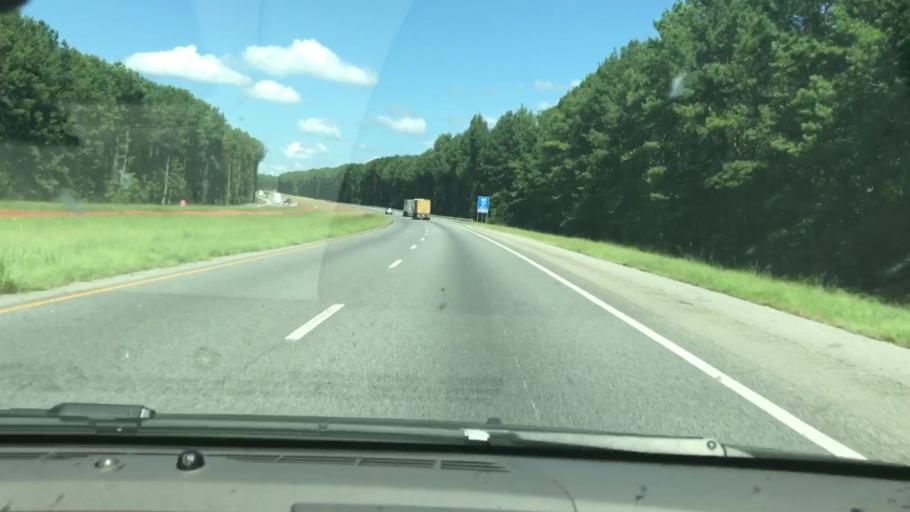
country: US
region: Georgia
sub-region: Harris County
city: Hamilton
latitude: 32.6934
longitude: -84.9944
